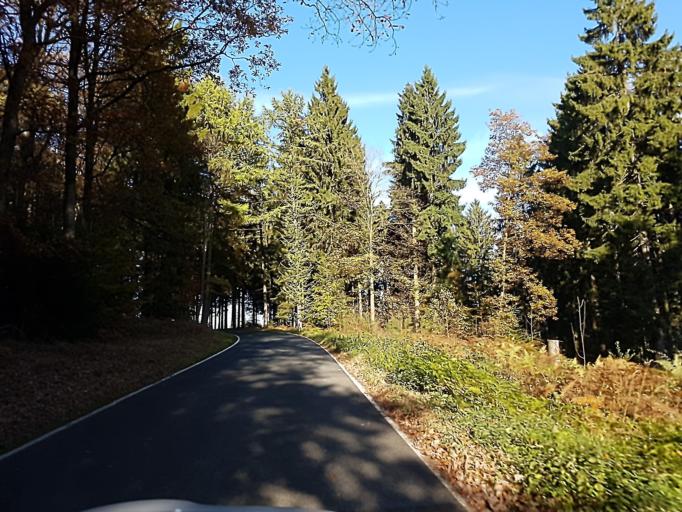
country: DE
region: North Rhine-Westphalia
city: Meinerzhagen
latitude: 51.0701
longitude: 7.6132
